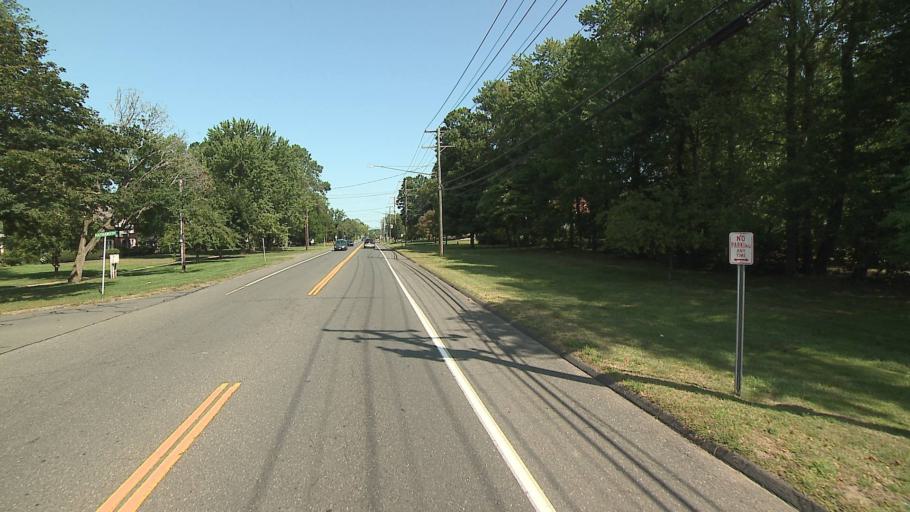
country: US
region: Connecticut
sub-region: Hartford County
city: Enfield
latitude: 41.9864
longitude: -72.5932
